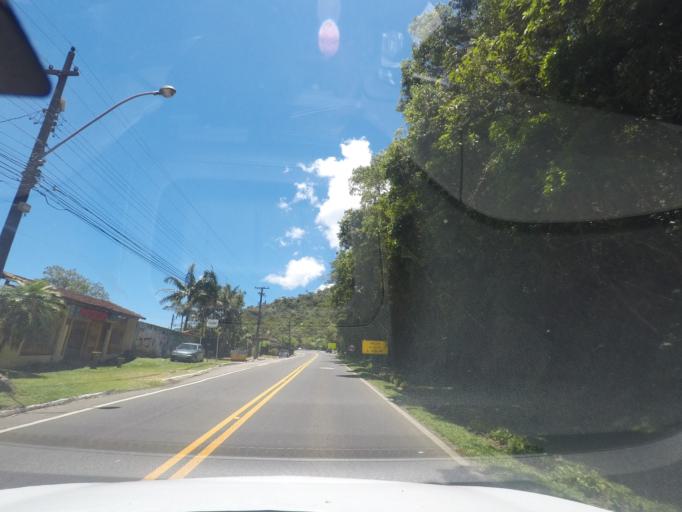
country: BR
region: Rio de Janeiro
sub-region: Teresopolis
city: Teresopolis
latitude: -22.4588
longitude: -42.9865
